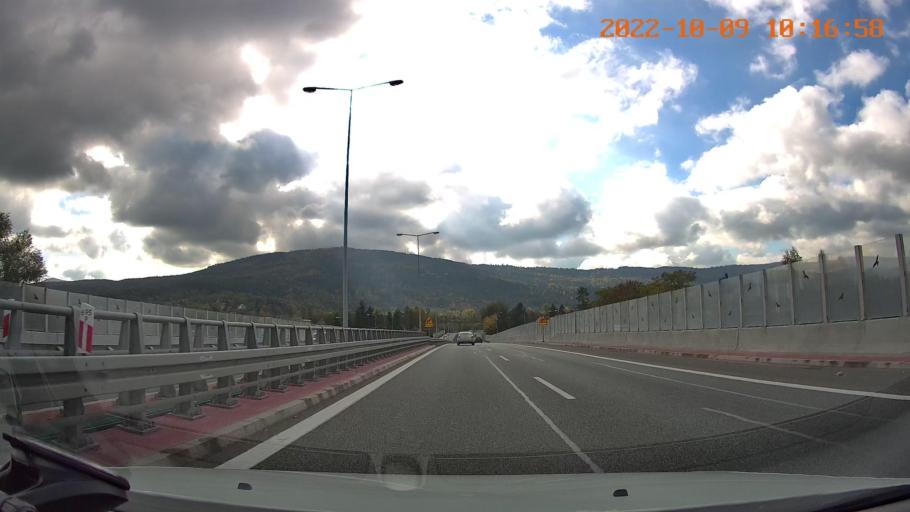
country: PL
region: Lesser Poland Voivodeship
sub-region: Powiat myslenicki
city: Myslenice
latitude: 49.8330
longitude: 19.9509
